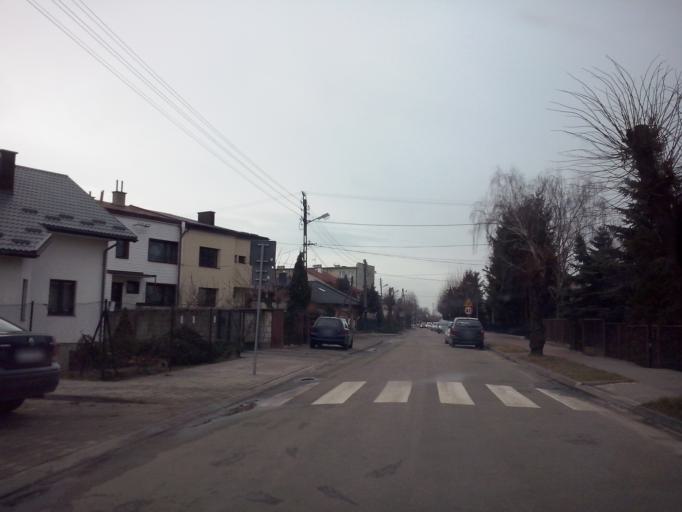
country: PL
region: Lublin Voivodeship
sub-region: Powiat bilgorajski
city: Bilgoraj
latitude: 50.5451
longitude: 22.7271
